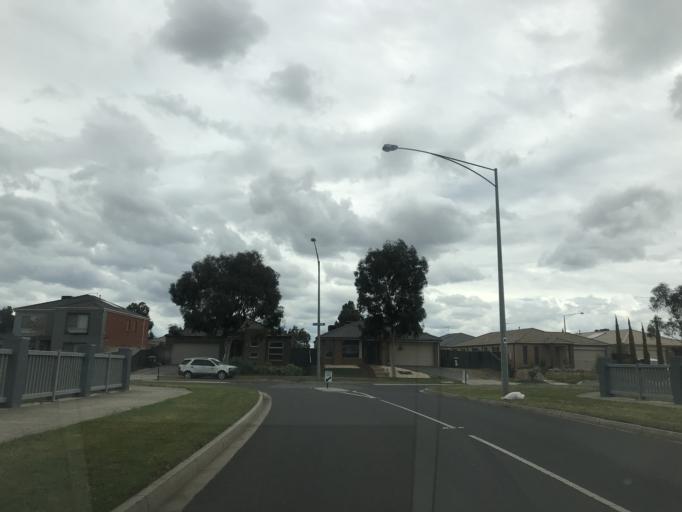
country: AU
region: Victoria
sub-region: Brimbank
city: Derrimut
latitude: -37.7917
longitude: 144.7554
